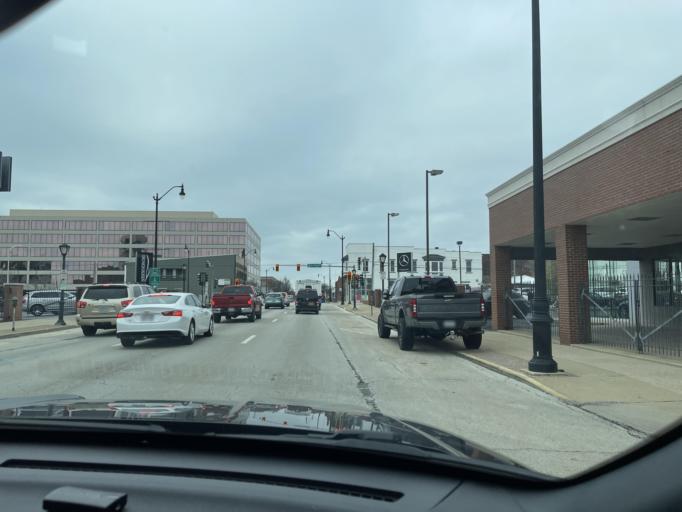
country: US
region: Illinois
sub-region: Sangamon County
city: Springfield
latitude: 39.8029
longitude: -89.6524
